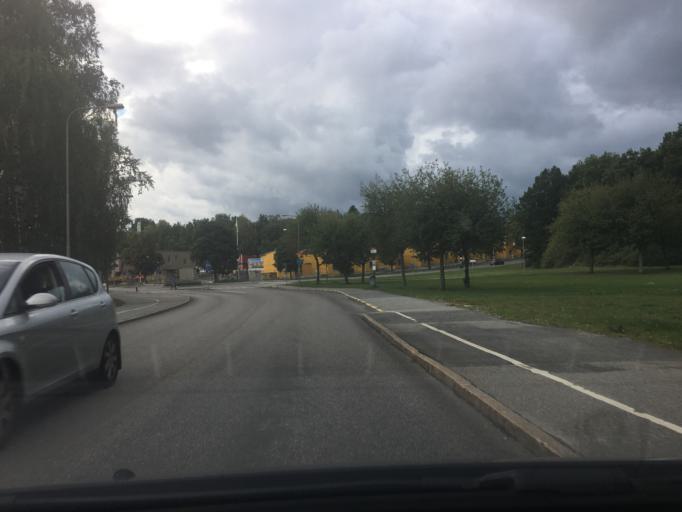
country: SE
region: Stockholm
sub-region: Stockholms Kommun
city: Bromma
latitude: 59.3670
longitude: 17.8885
